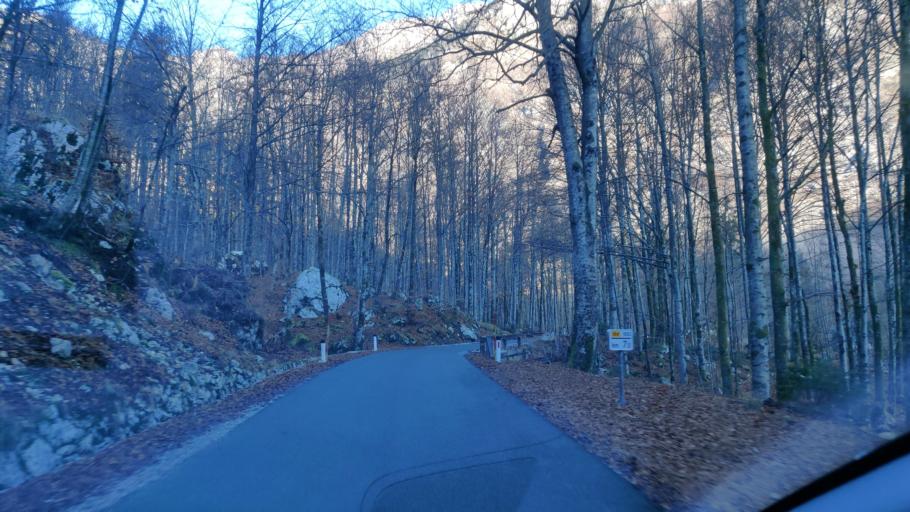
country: SI
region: Tolmin
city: Tolmin
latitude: 46.2825
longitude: 13.8081
